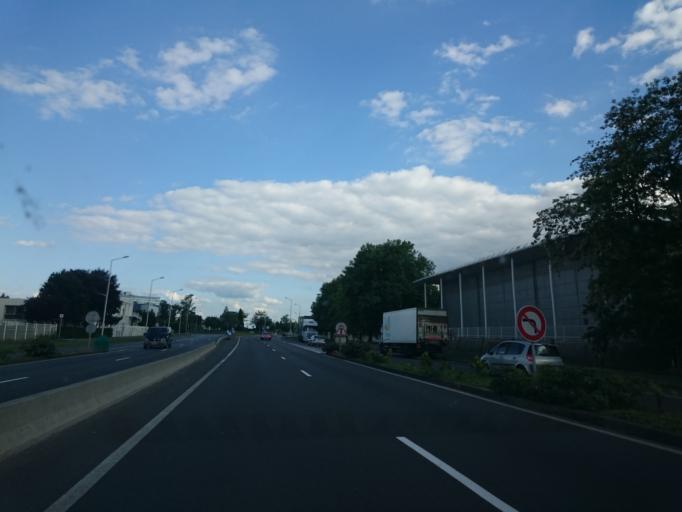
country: FR
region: Ile-de-France
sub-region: Departement de l'Essonne
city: Evry
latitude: 48.6216
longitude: 2.4496
